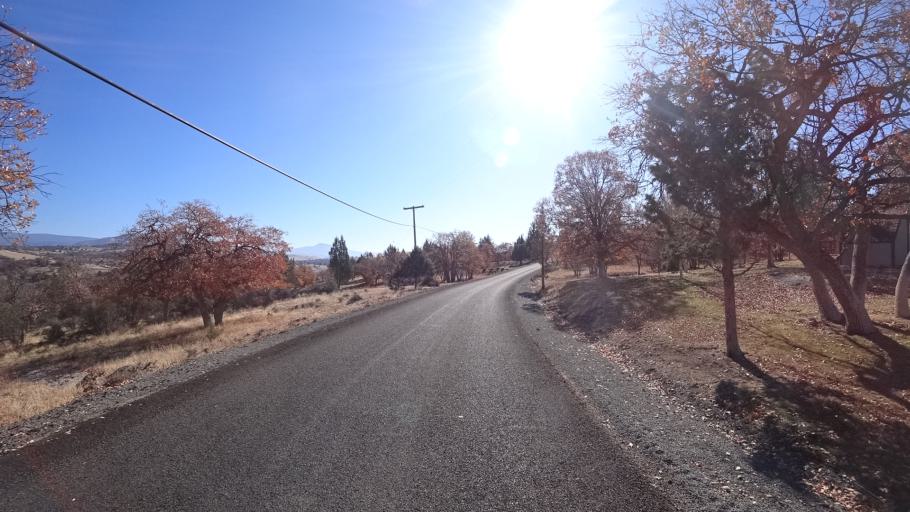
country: US
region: California
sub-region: Siskiyou County
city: Montague
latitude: 41.8793
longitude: -122.4824
